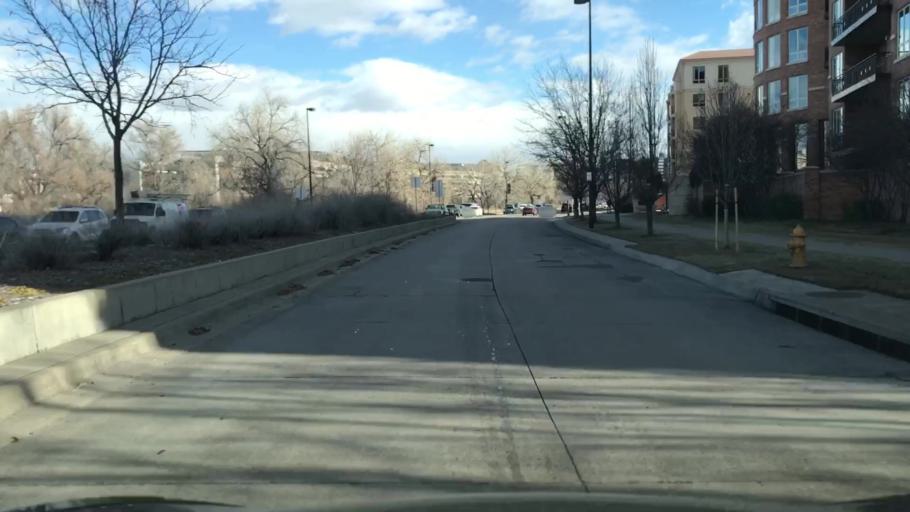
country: US
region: Colorado
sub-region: Arapahoe County
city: Glendale
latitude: 39.7154
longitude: -104.9588
